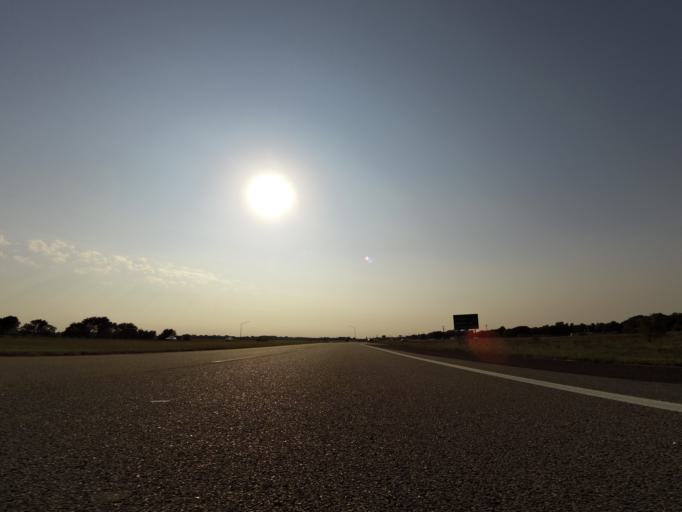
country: US
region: Kansas
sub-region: Reno County
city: Haven
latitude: 37.8947
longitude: -97.7720
